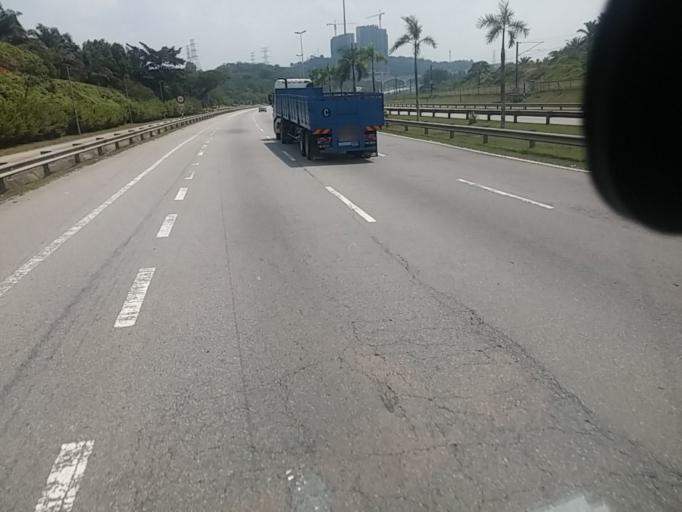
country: MY
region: Putrajaya
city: Putrajaya
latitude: 2.9507
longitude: 101.6590
